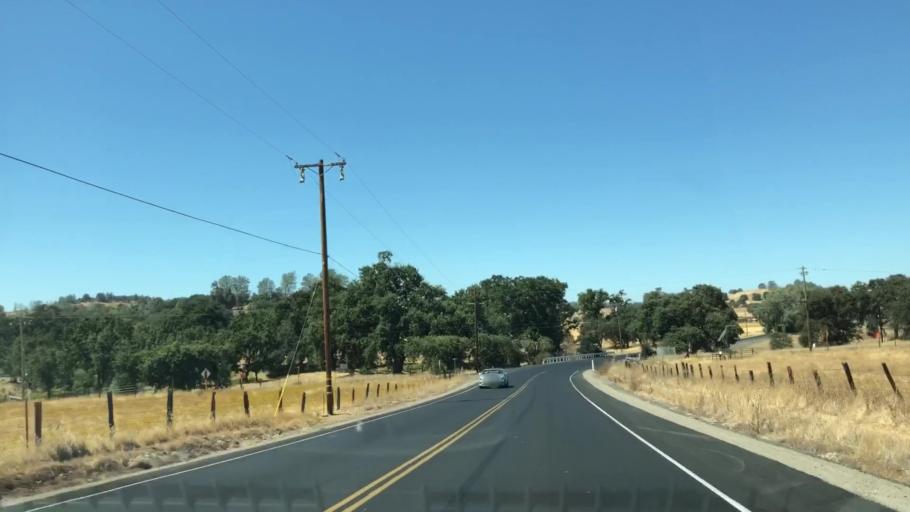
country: US
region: California
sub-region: Tuolumne County
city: Jamestown
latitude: 37.8777
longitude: -120.4474
